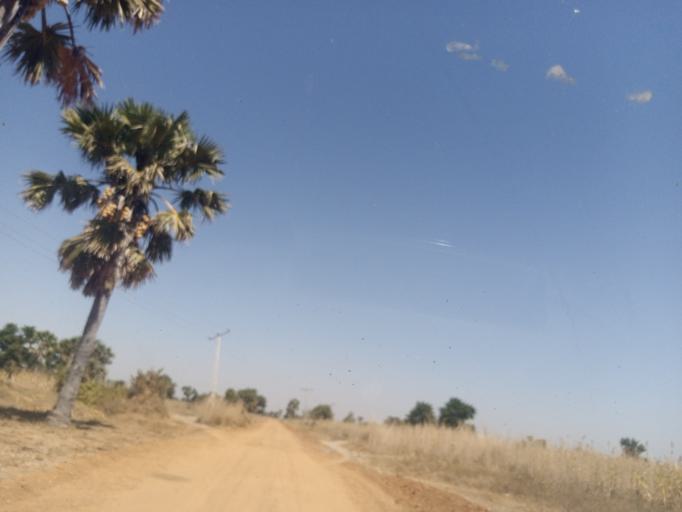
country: NG
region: Adamawa
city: Yola
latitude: 9.2975
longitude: 12.8872
